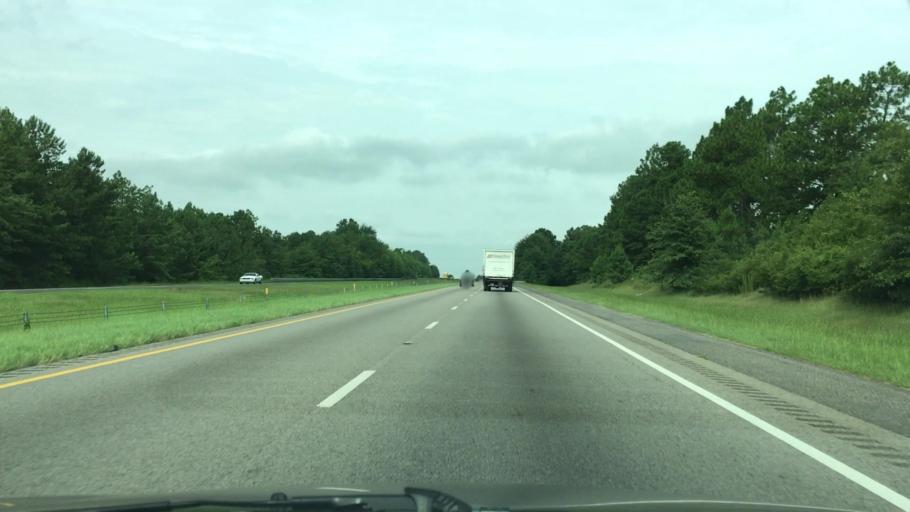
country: US
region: South Carolina
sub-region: Aiken County
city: Graniteville
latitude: 33.6342
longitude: -81.7785
